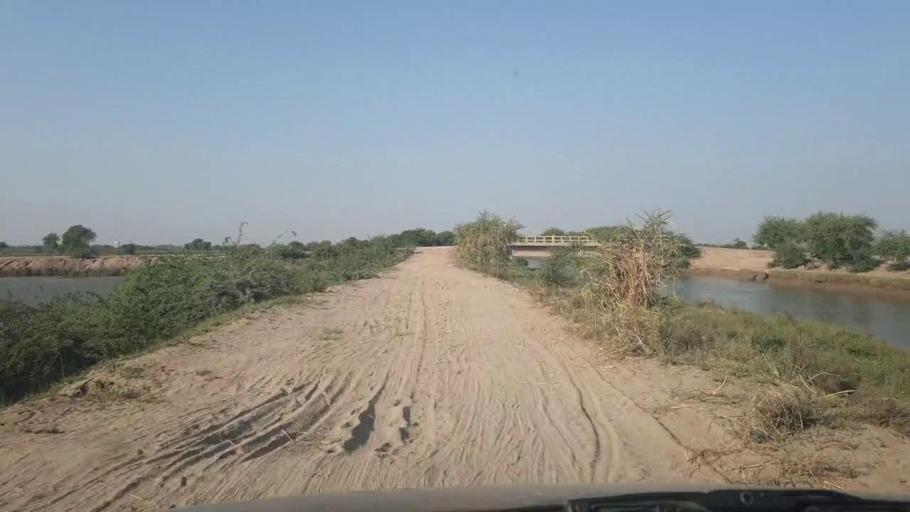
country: PK
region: Sindh
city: Badin
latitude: 24.6385
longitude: 68.8150
